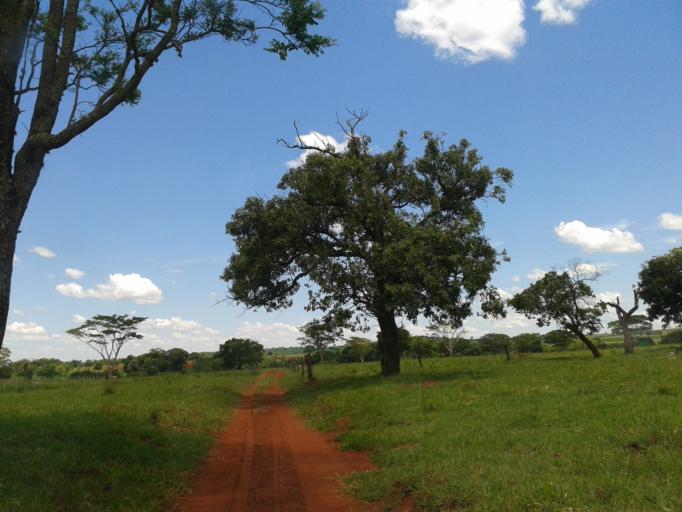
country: BR
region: Minas Gerais
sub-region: Centralina
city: Centralina
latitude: -18.7059
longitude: -49.1764
